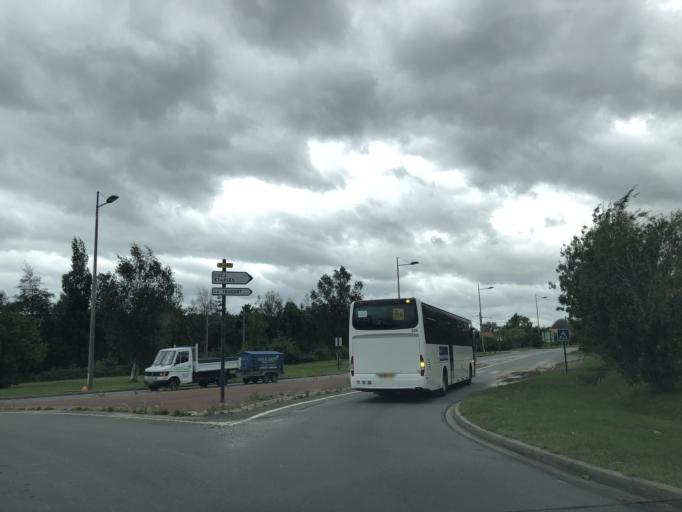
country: FR
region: Nord-Pas-de-Calais
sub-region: Departement du Pas-de-Calais
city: Saint-Josse
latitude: 50.4635
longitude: 1.6491
